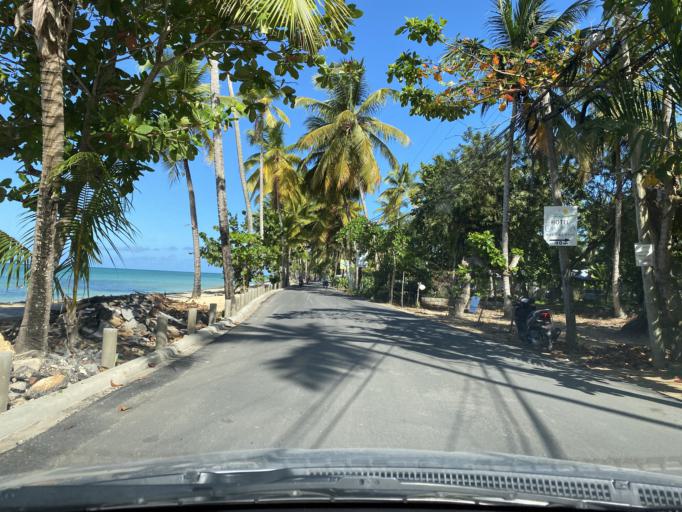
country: DO
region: Samana
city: Las Terrenas
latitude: 19.3235
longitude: -69.5319
